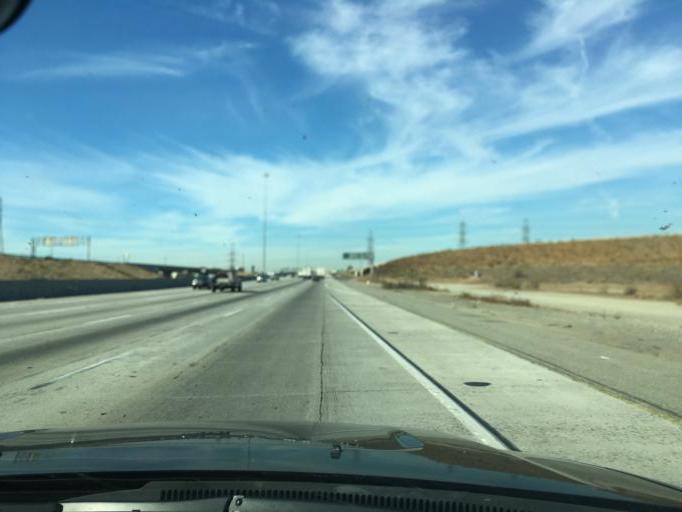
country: US
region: California
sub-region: Riverside County
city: Mira Loma
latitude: 34.0223
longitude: -117.5515
